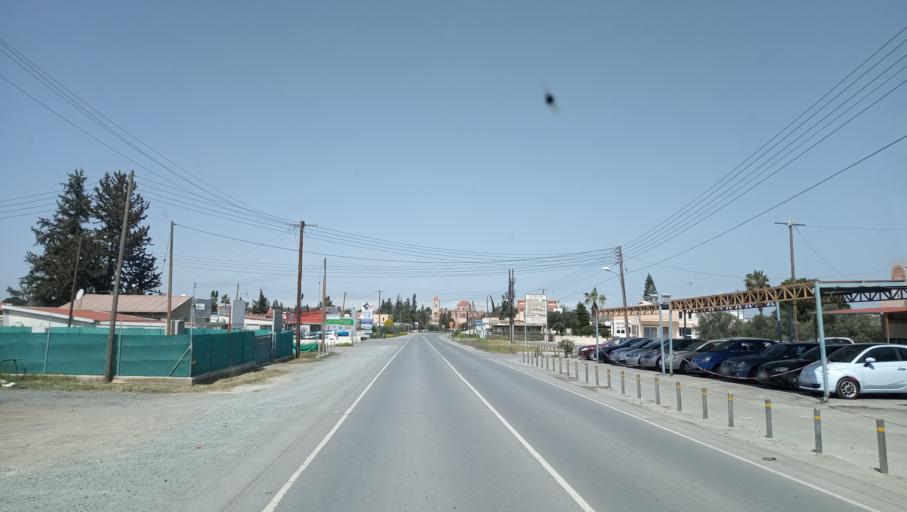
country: CY
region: Lefkosia
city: Alampra
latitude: 35.0093
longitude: 33.3938
